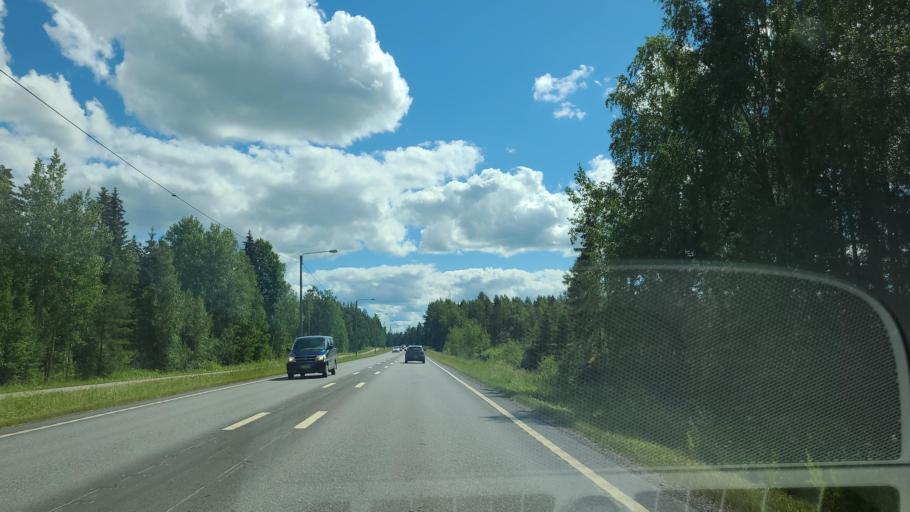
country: FI
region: Ostrobothnia
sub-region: Kyroenmaa
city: Isokyroe
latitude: 62.9840
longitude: 22.3331
